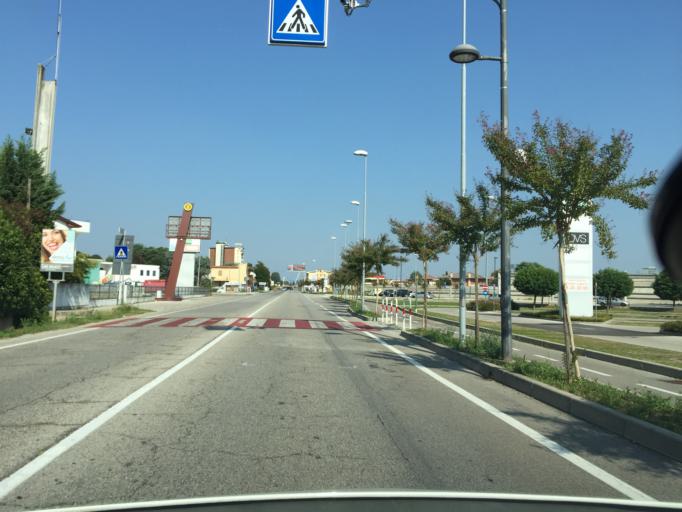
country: IT
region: Veneto
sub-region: Provincia di Padova
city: Fontaniva
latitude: 45.6426
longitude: 11.7653
